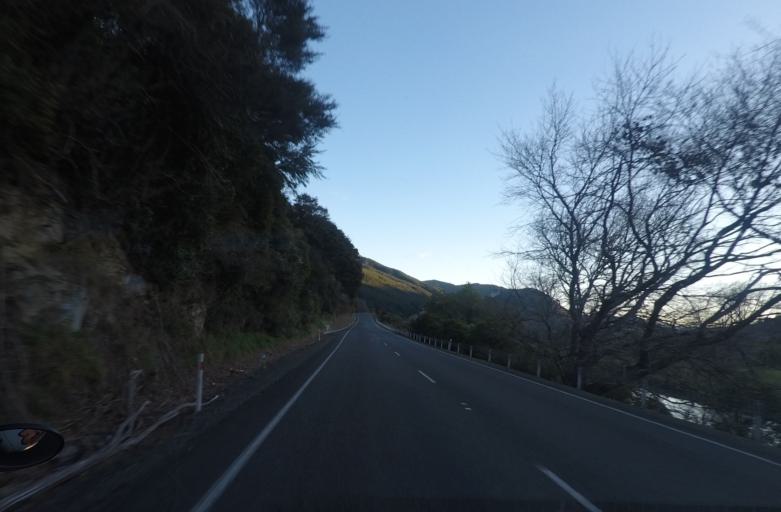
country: NZ
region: Marlborough
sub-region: Marlborough District
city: Picton
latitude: -41.2761
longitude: 173.7311
